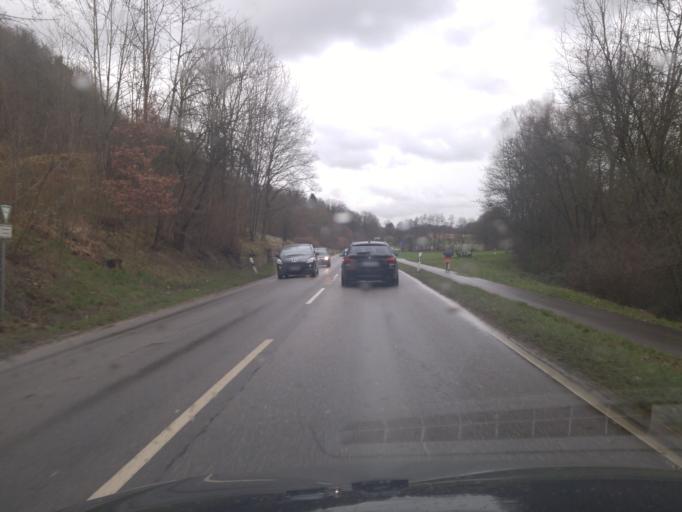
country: DE
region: Baden-Wuerttemberg
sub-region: Regierungsbezirk Stuttgart
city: Steinheim am der Murr
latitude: 48.9612
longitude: 9.2890
